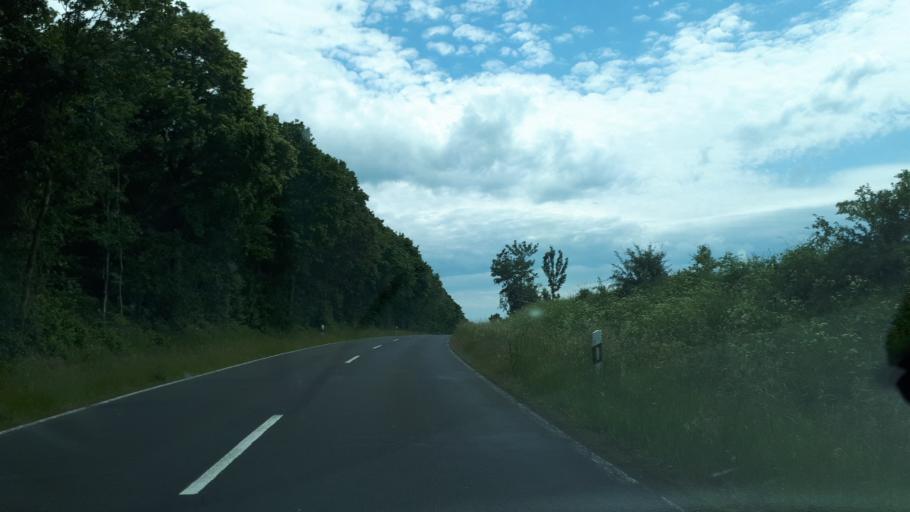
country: DE
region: Rheinland-Pfalz
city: Strohn
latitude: 50.1281
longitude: 6.9179
